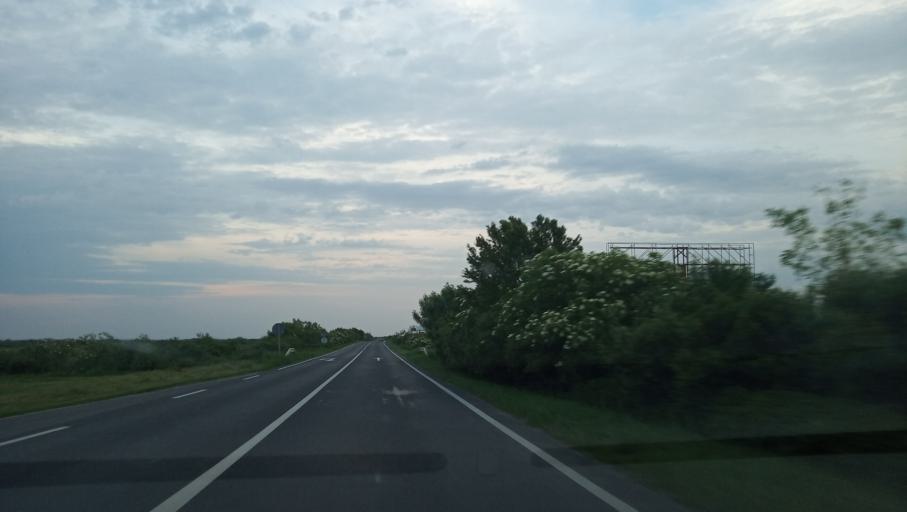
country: RO
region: Timis
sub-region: Comuna Voiteg
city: Voiteg
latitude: 45.4860
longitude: 21.2340
